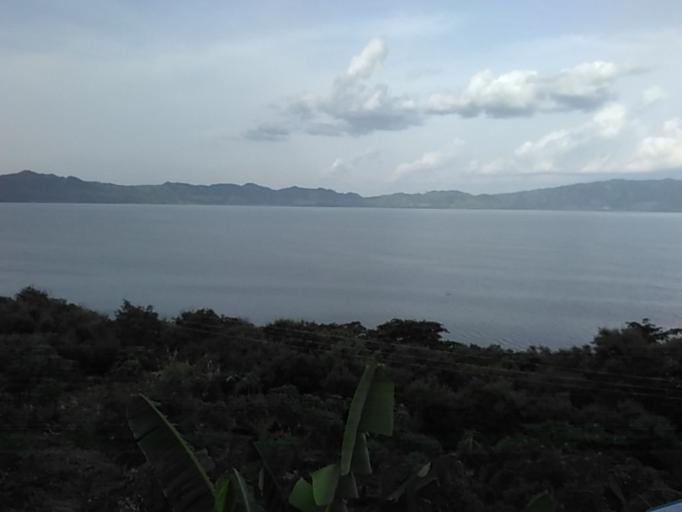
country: GH
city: Bekwai
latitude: 6.5178
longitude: -1.4410
